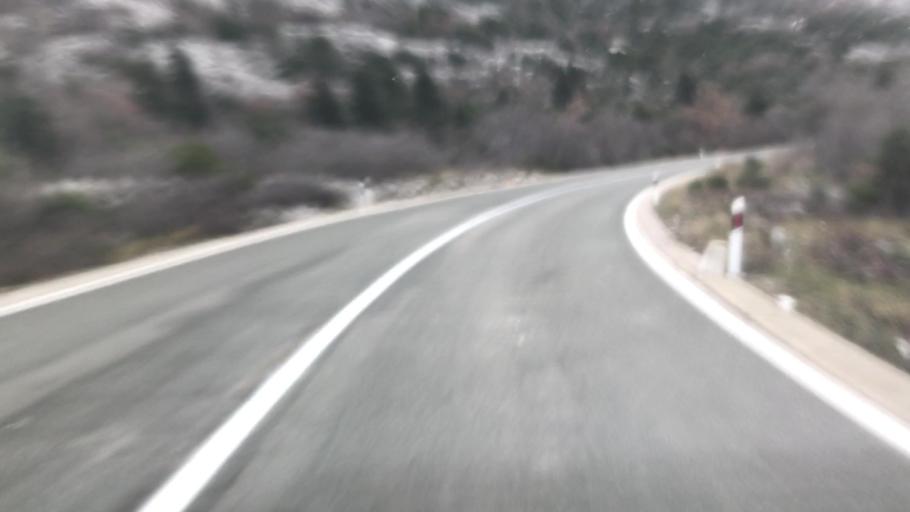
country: HR
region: Licko-Senjska
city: Novalja
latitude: 44.6625
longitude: 14.9480
